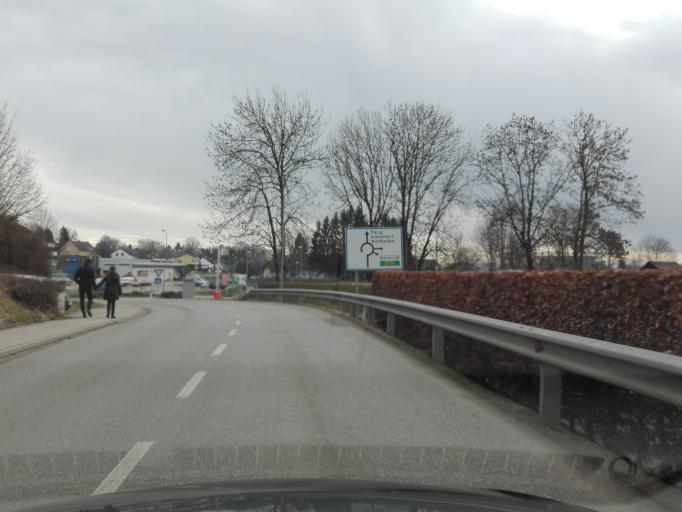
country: AT
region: Upper Austria
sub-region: Politischer Bezirk Perg
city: Perg
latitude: 48.2692
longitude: 14.5829
